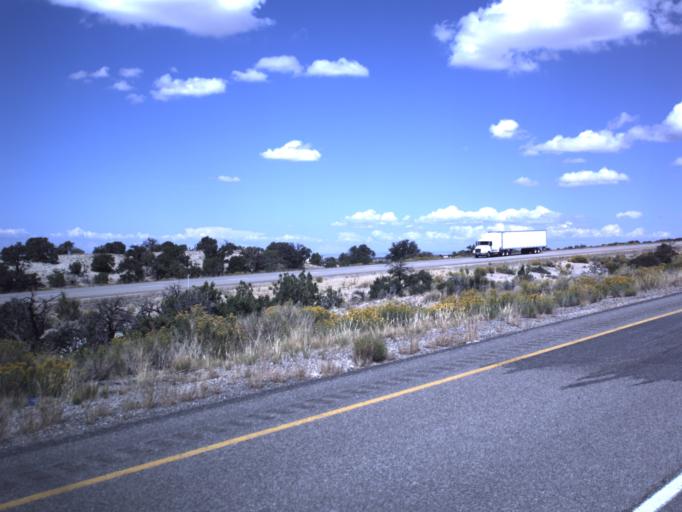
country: US
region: Utah
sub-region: Emery County
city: Ferron
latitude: 38.8437
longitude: -110.9486
